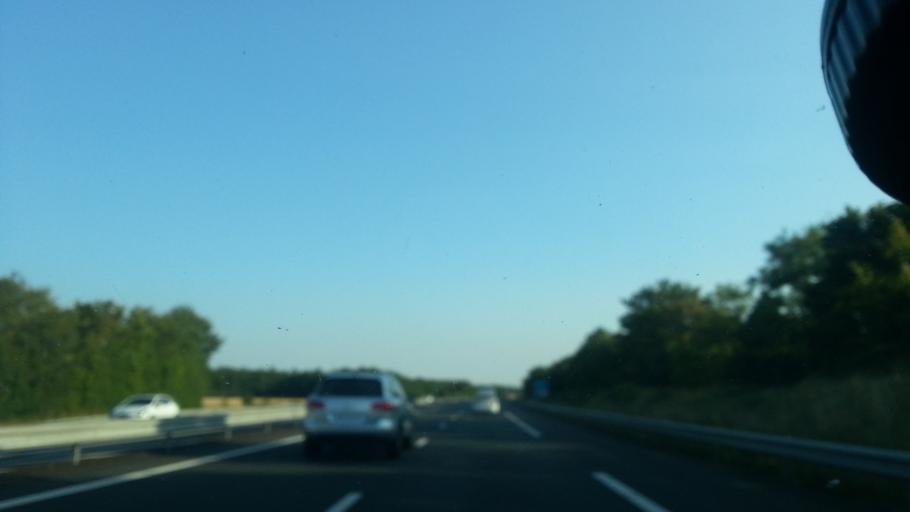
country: FR
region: Poitou-Charentes
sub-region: Departement des Deux-Sevres
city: Beauvoir-sur-Niort
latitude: 46.0990
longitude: -0.5349
